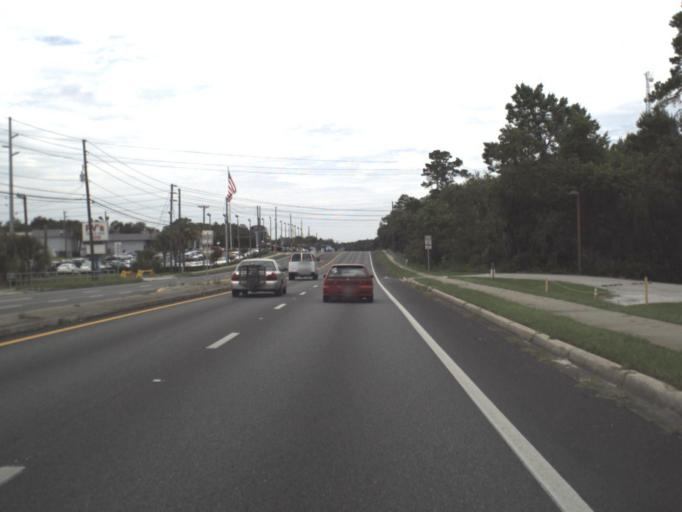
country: US
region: Florida
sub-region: Citrus County
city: Inverness Highlands North
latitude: 28.8441
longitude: -82.3660
